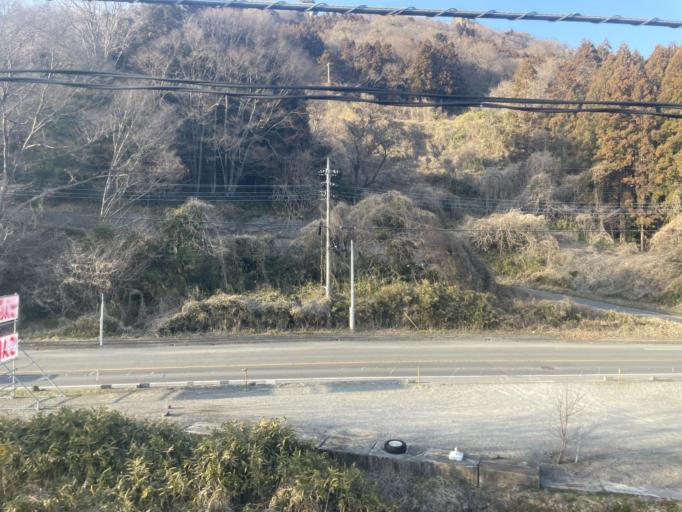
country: JP
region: Gunma
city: Nakanojomachi
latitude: 36.5571
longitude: 138.9066
